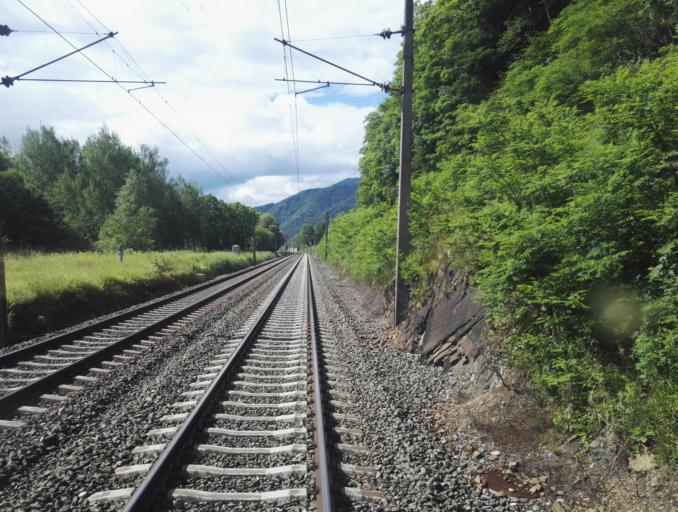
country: AT
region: Styria
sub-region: Politischer Bezirk Bruck-Muerzzuschlag
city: Pernegg an der Mur
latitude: 47.3465
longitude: 15.3518
